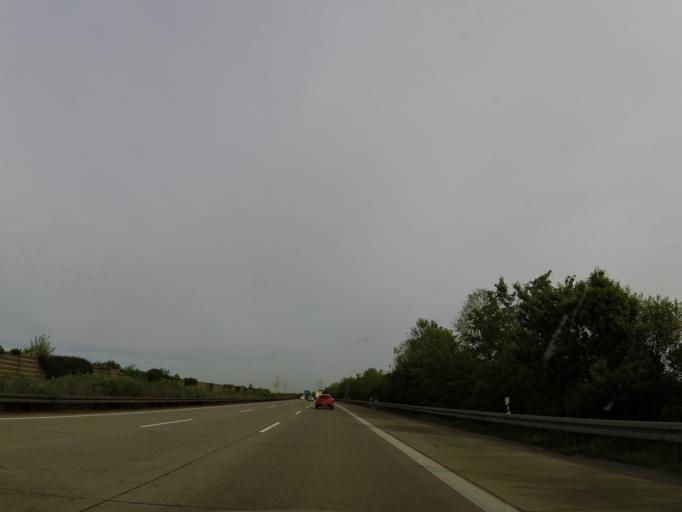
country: DE
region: Lower Saxony
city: Algermissen
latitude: 52.2797
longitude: 9.9088
